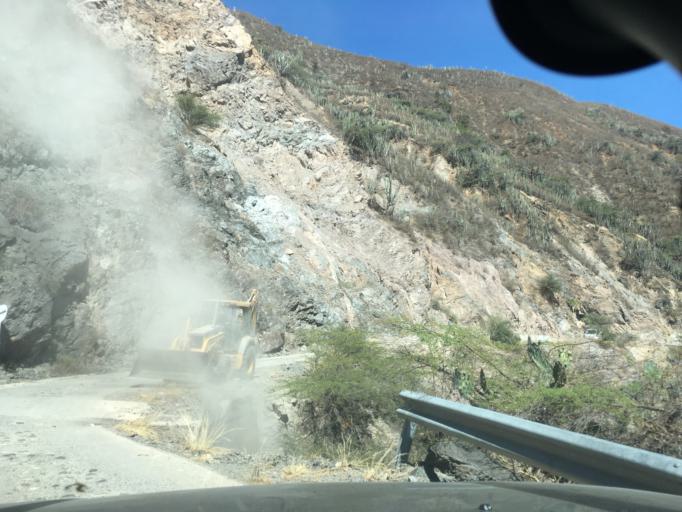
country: CO
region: Santander
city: Aratoca
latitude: 6.7659
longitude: -72.9835
